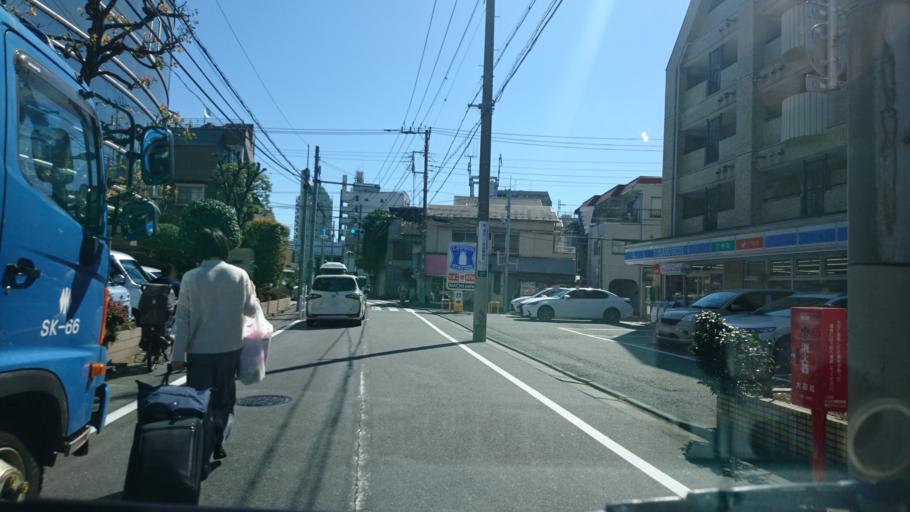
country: JP
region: Kanagawa
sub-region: Kawasaki-shi
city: Kawasaki
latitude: 35.5692
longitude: 139.7281
